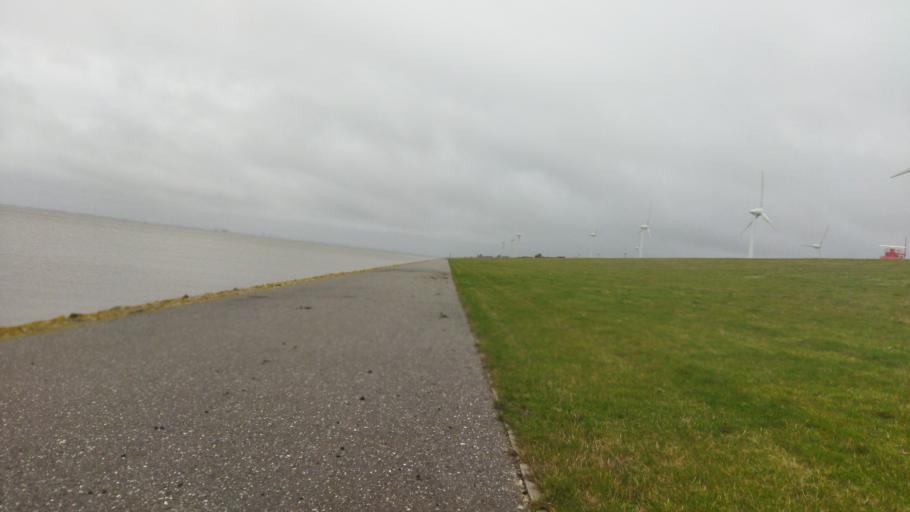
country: DE
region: Lower Saxony
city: Emden
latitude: 53.3350
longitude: 7.1114
